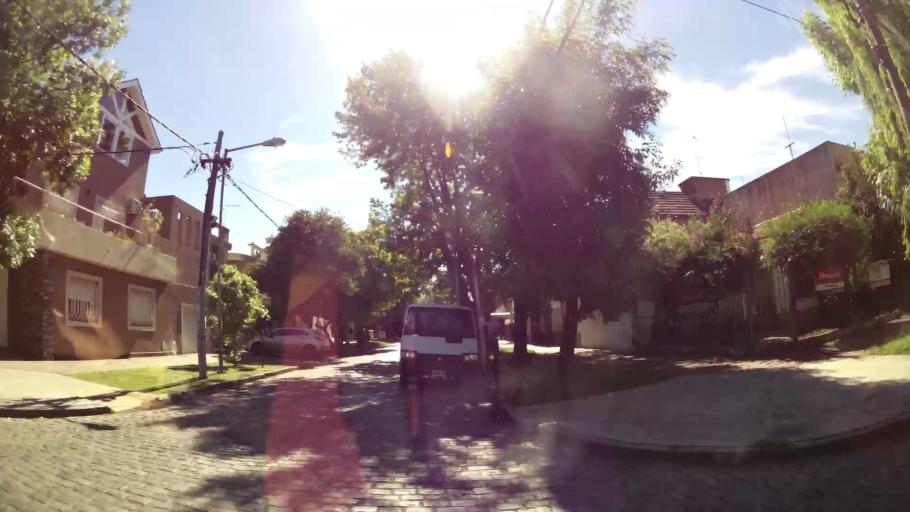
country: AR
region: Buenos Aires
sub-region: Partido de Lomas de Zamora
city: Lomas de Zamora
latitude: -34.7460
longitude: -58.4012
